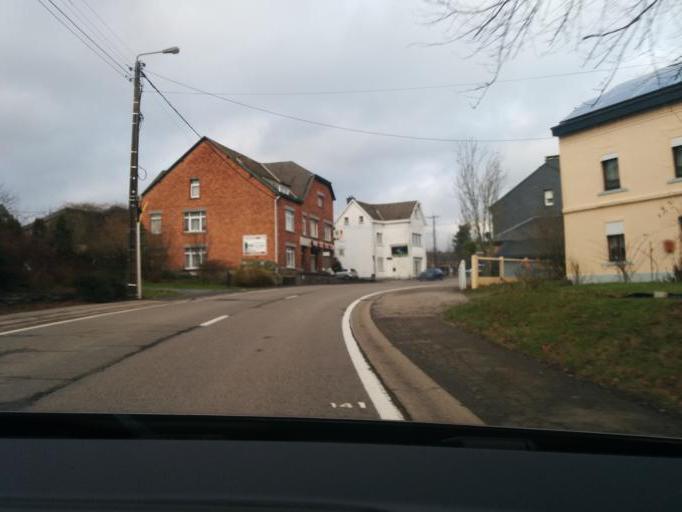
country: BE
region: Wallonia
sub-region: Province du Luxembourg
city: Gouvy
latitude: 50.1907
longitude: 5.9507
